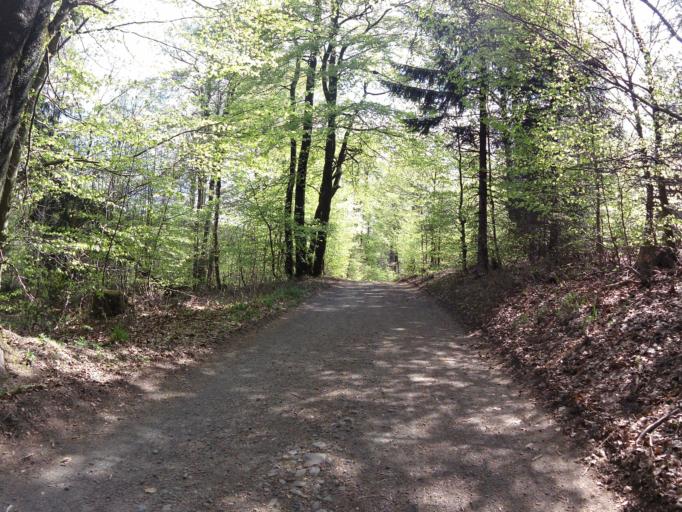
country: DE
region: Thuringia
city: Pappenheim
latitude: 50.7864
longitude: 10.5379
